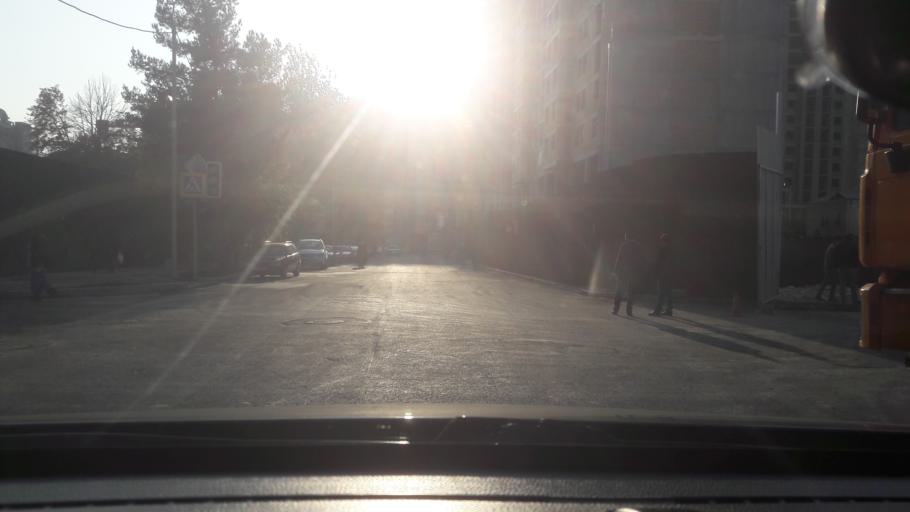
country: TJ
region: Dushanbe
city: Dushanbe
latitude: 38.5732
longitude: 68.7969
